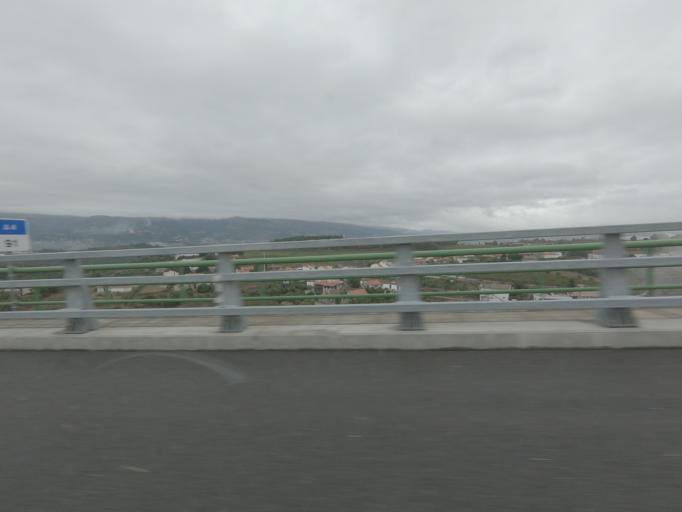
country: PT
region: Vila Real
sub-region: Vila Real
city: Vila Real
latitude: 41.2776
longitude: -7.7412
